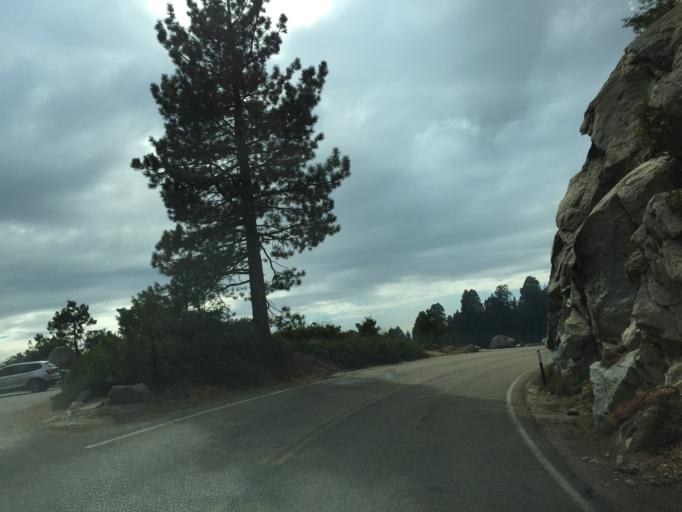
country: US
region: California
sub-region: Tulare County
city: Three Rivers
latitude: 36.7189
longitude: -118.9182
